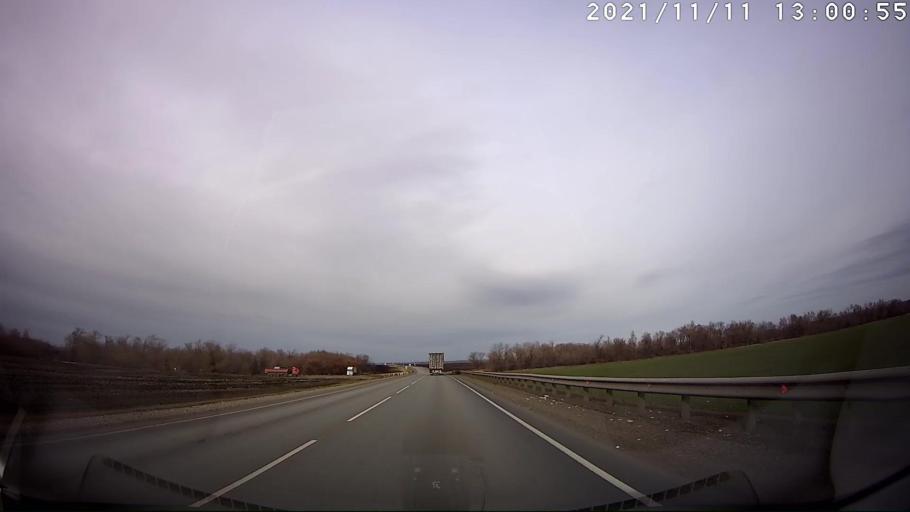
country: RU
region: Ulyanovsk
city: Isheyevka
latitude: 54.3760
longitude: 48.2015
